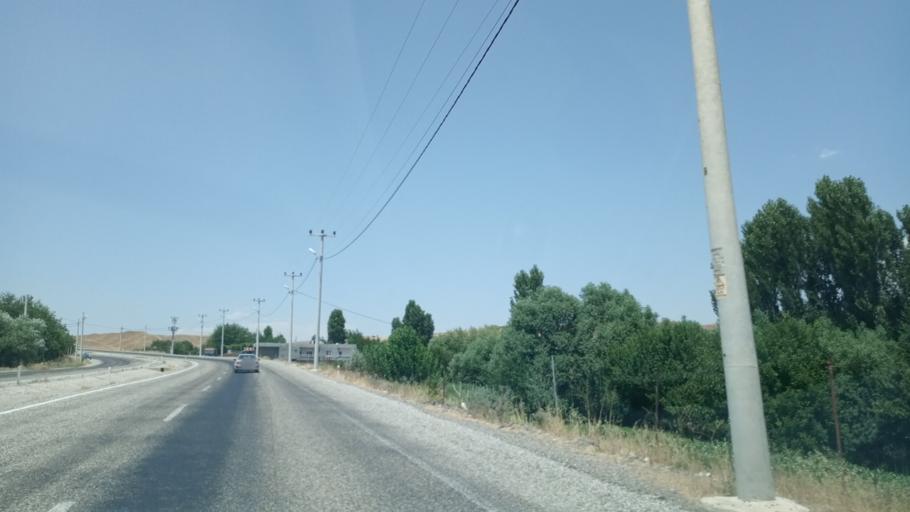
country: TR
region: Batman
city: Bekirhan
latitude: 38.1440
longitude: 41.2873
